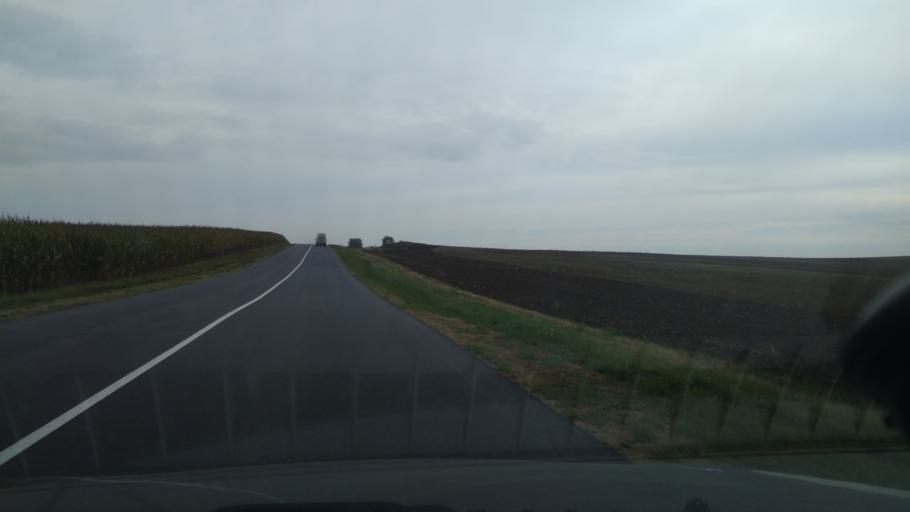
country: BY
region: Minsk
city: Rudzyensk
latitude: 53.6151
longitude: 27.7521
